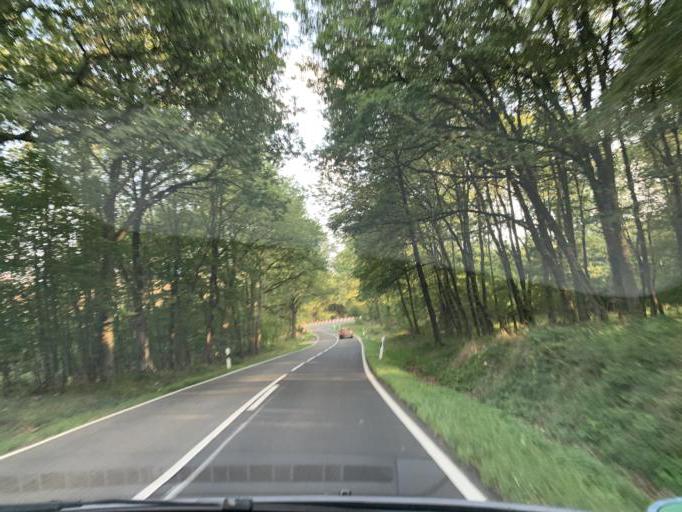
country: DE
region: North Rhine-Westphalia
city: Heimbach
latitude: 50.6490
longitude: 6.4507
